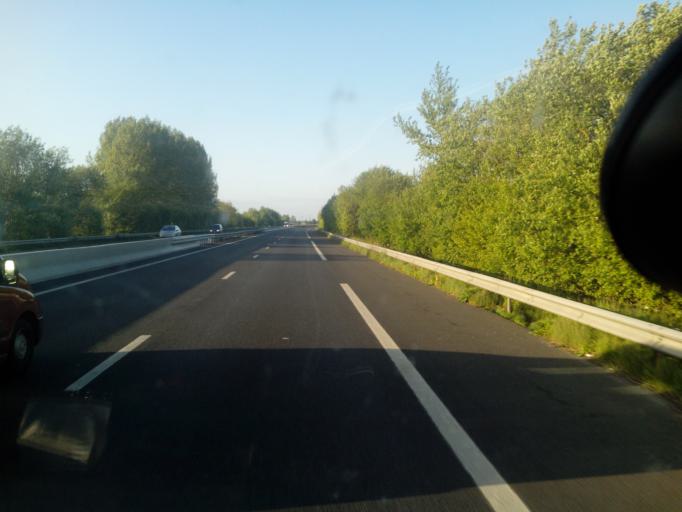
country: FR
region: Haute-Normandie
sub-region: Departement de la Seine-Maritime
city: Saint-Saens
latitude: 49.6902
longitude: 1.3532
